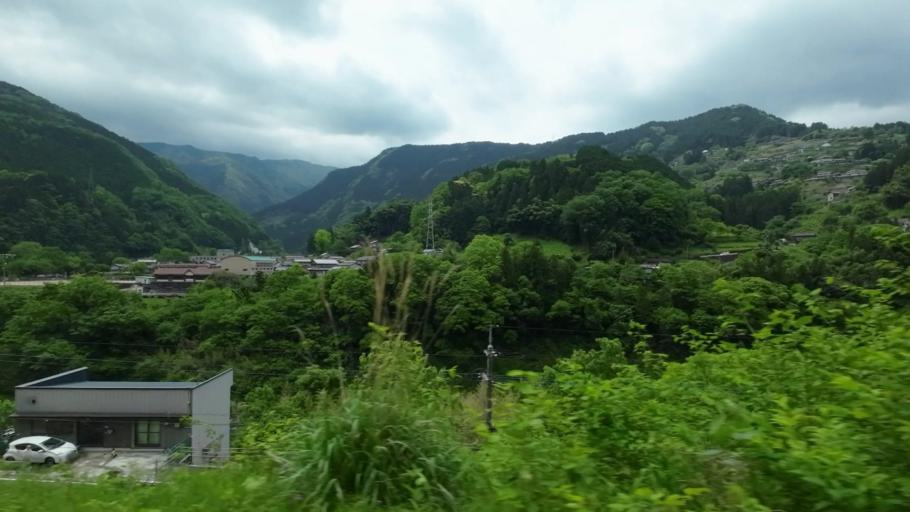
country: JP
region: Tokushima
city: Ikedacho
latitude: 33.9706
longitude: 133.7734
